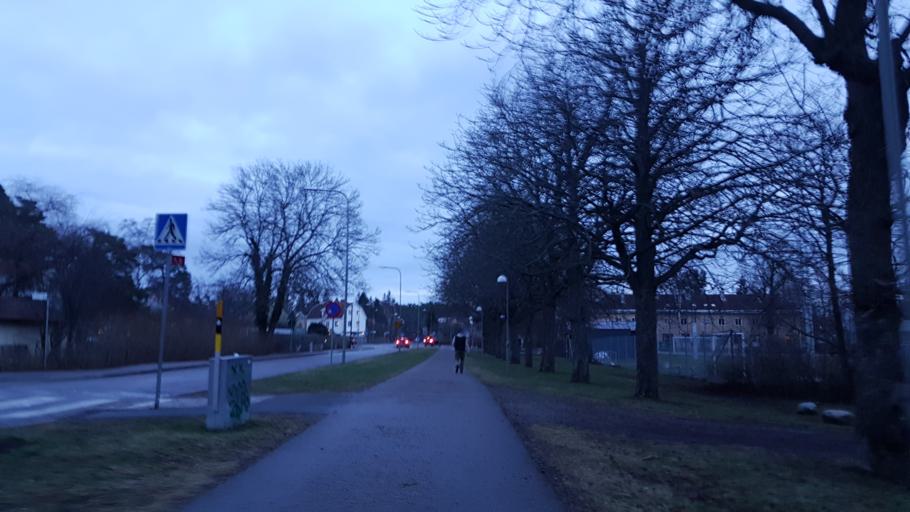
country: SE
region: Stockholm
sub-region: Stockholms Kommun
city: Arsta
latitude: 59.2808
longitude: 18.0487
